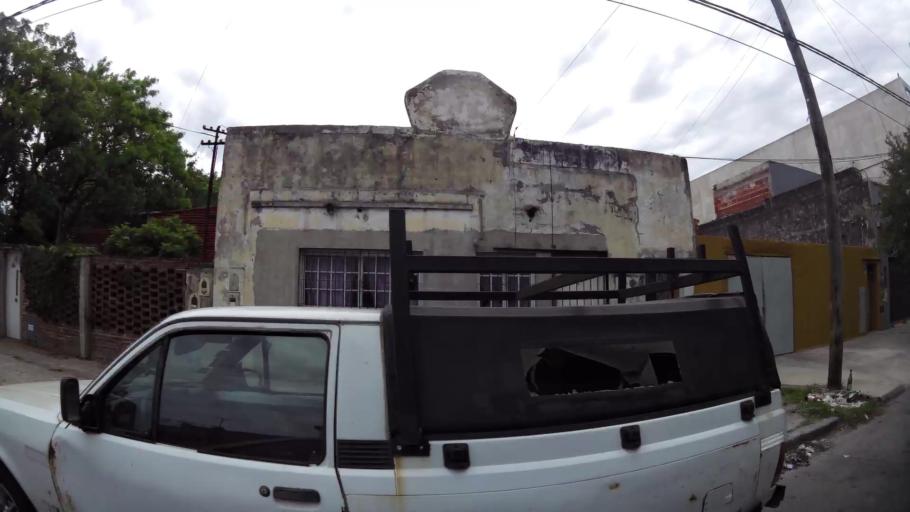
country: AR
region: Buenos Aires
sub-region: Partido de Lanus
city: Lanus
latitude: -34.6806
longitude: -58.3911
